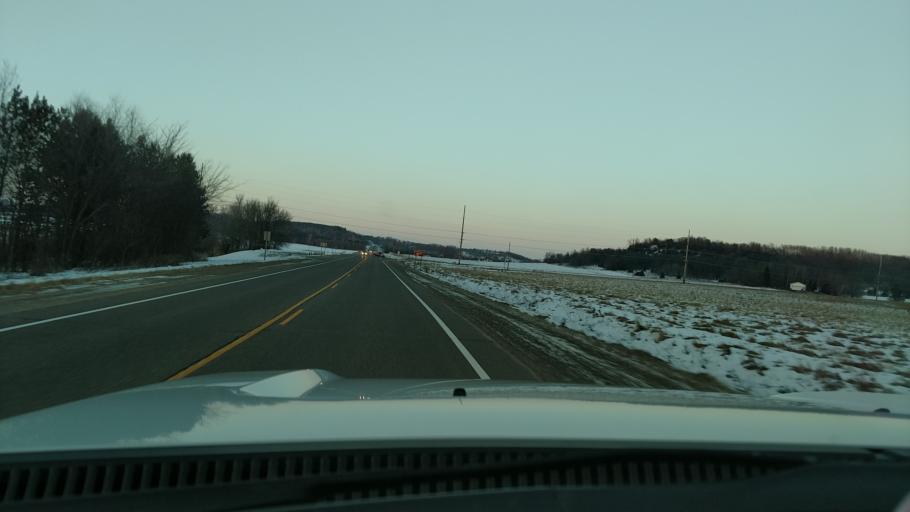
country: US
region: Wisconsin
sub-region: Saint Croix County
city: Roberts
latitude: 44.9105
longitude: -92.5582
